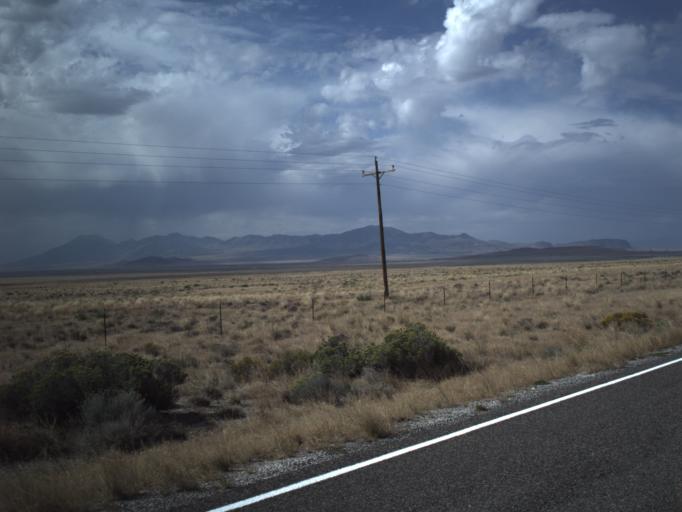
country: US
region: Utah
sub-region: Tooele County
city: Wendover
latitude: 41.4339
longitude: -113.7714
